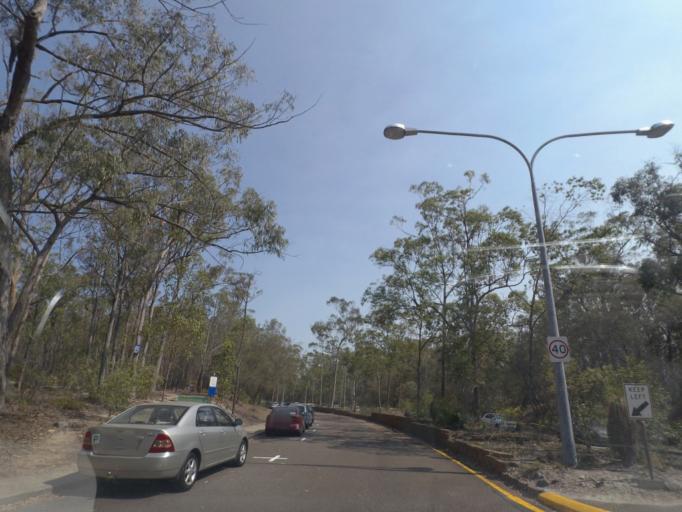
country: AU
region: Queensland
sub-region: Brisbane
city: Nathan
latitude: -27.5504
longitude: 153.0486
